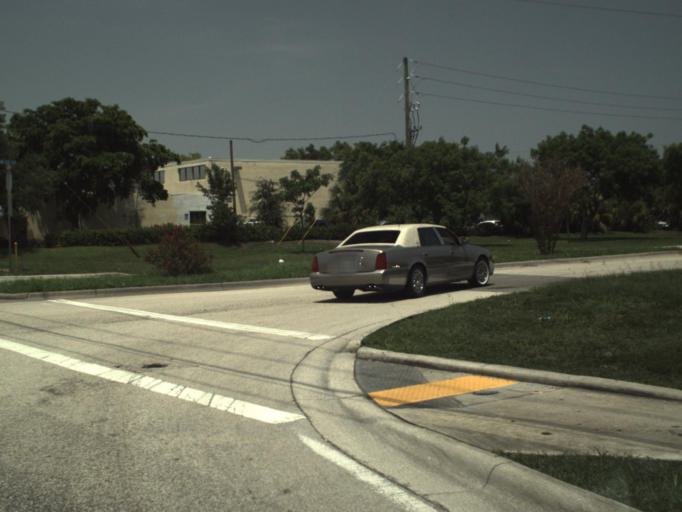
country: US
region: Florida
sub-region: Broward County
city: Pompano Beach
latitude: 26.2453
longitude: -80.1515
